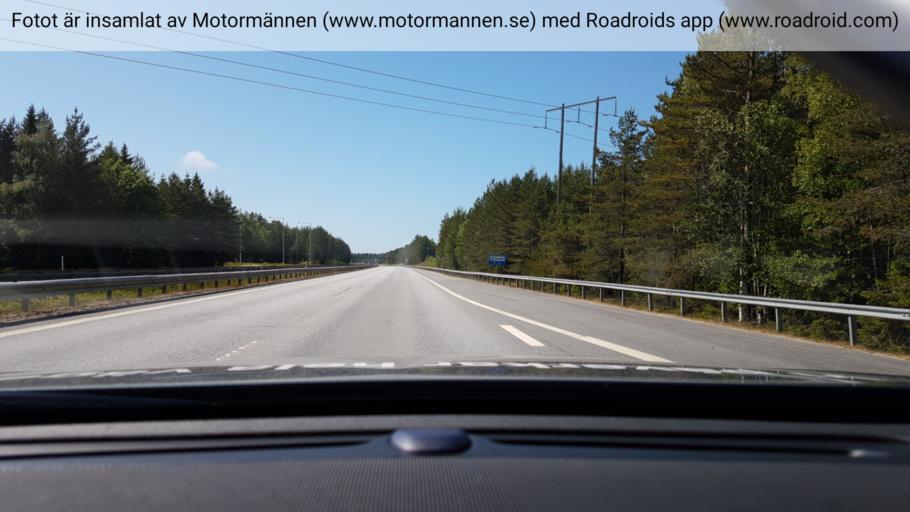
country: SE
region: Vaesterbotten
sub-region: Umea Kommun
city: Roback
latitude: 63.7859
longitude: 20.2009
